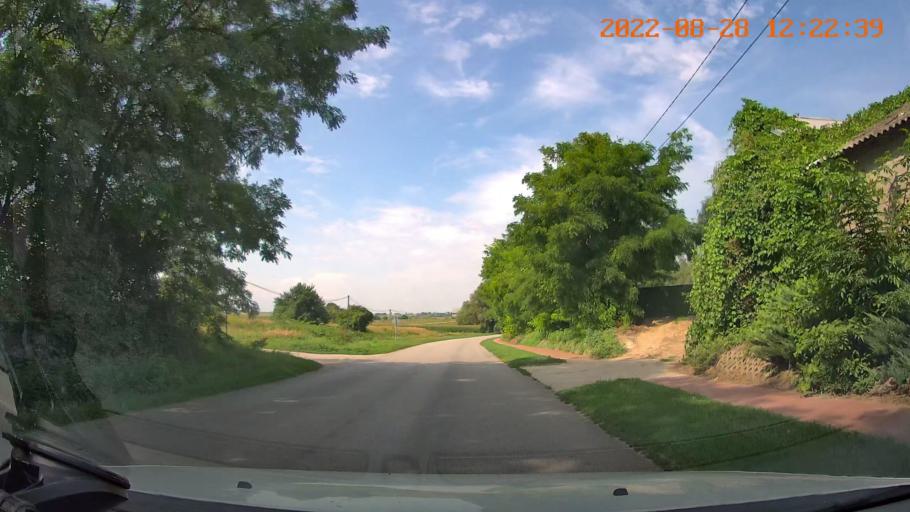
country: PL
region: Swietokrzyskie
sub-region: Powiat pinczowski
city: Zlota
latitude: 50.4171
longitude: 20.5496
